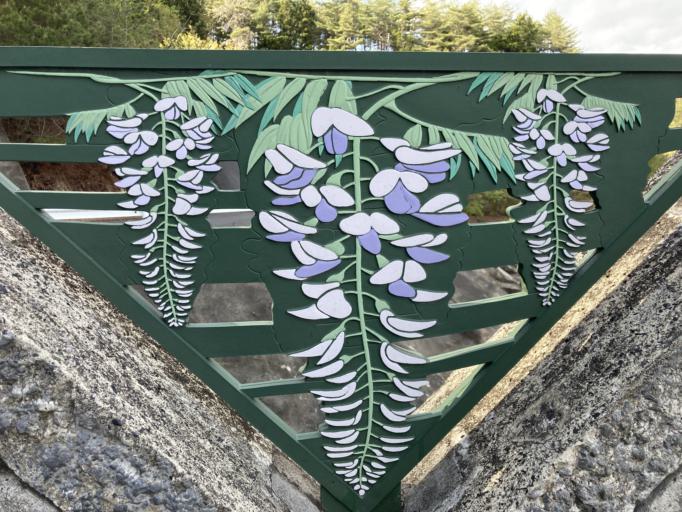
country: JP
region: Iwate
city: Ichinoseki
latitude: 38.8008
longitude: 141.4129
